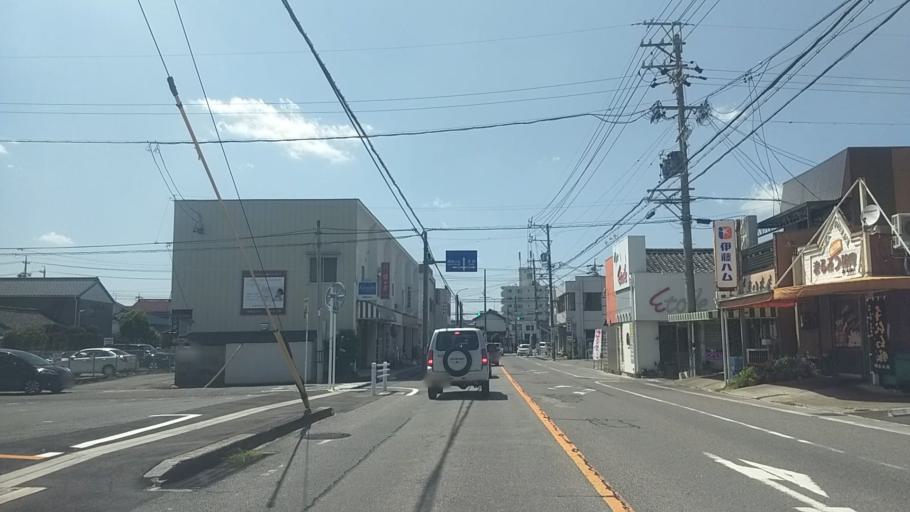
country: JP
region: Aichi
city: Okazaki
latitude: 34.9823
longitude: 137.1710
